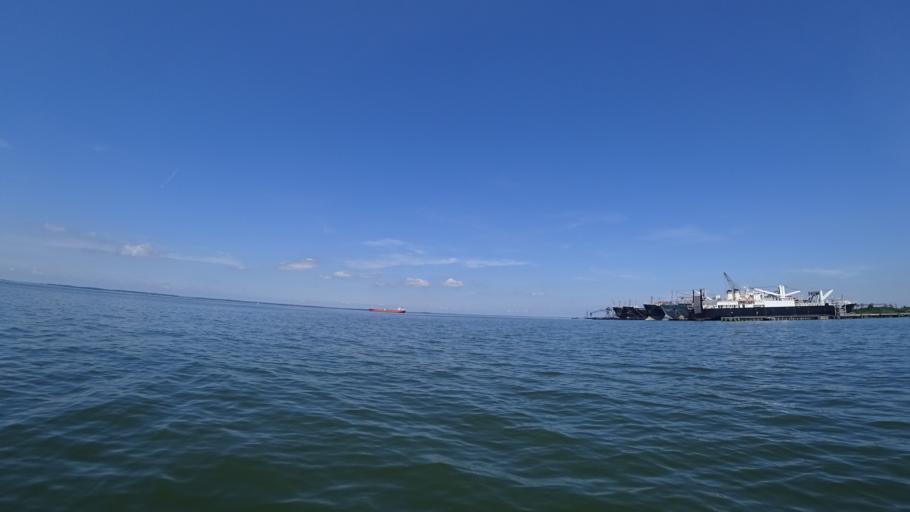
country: US
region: Virginia
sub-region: City of Newport News
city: Newport News
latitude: 36.9581
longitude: -76.4141
